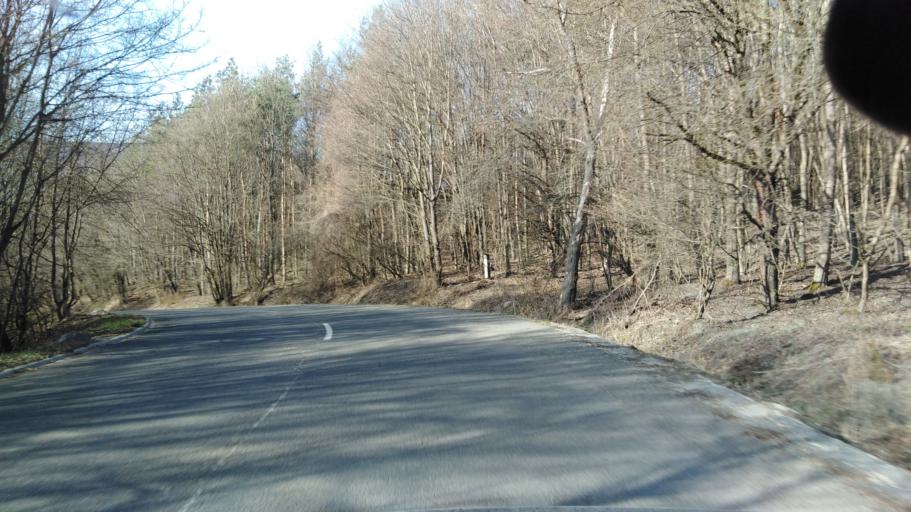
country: HU
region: Nograd
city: Somoskoujfalu
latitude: 48.1580
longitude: 19.8505
